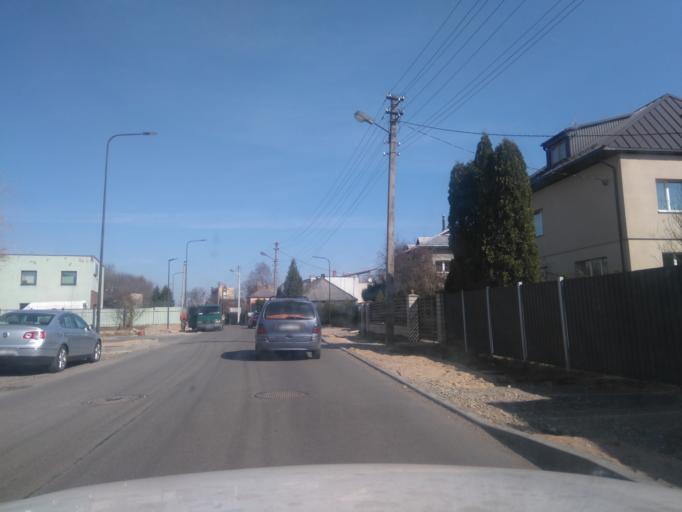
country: LT
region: Kauno apskritis
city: Dainava (Kaunas)
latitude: 54.8879
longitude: 23.9542
